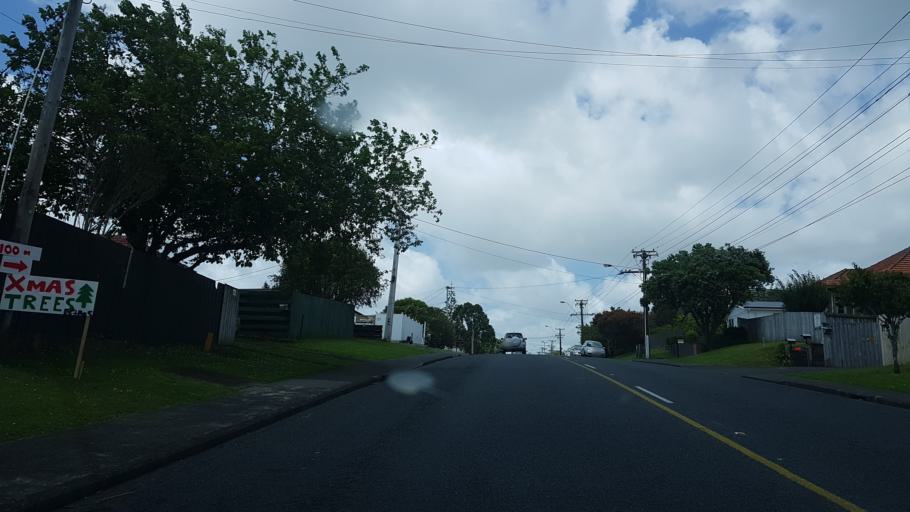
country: NZ
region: Auckland
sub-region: Auckland
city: North Shore
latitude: -36.8026
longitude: 174.7037
